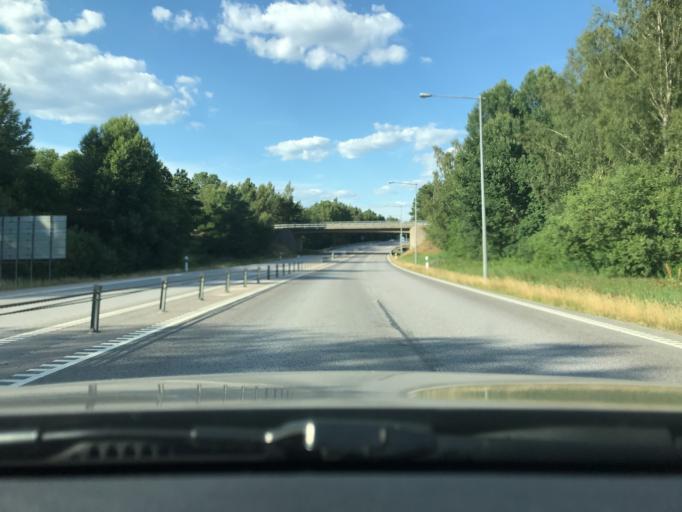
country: SE
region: Kronoberg
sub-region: Vaxjo Kommun
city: Vaexjoe
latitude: 56.8862
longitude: 14.7475
